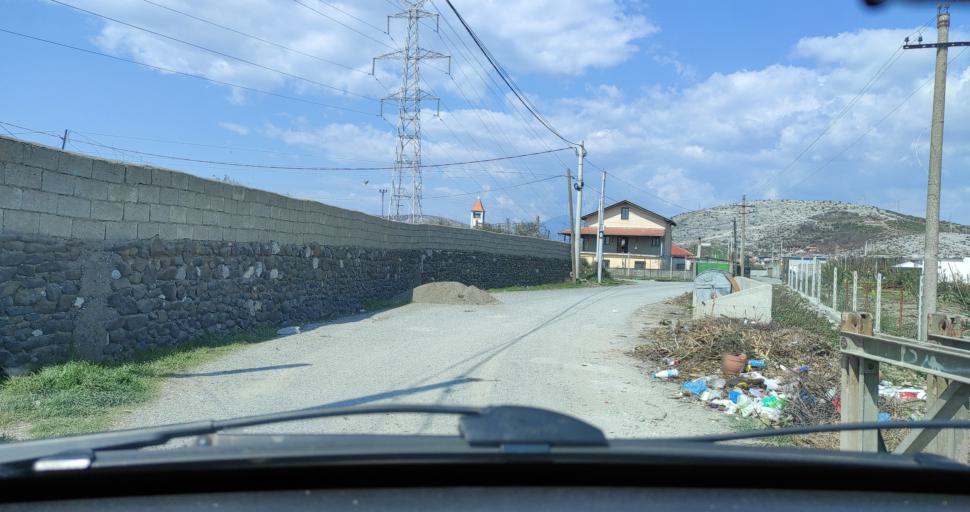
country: AL
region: Shkoder
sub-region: Rrethi i Shkodres
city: Vau i Dejes
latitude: 42.0044
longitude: 19.6419
